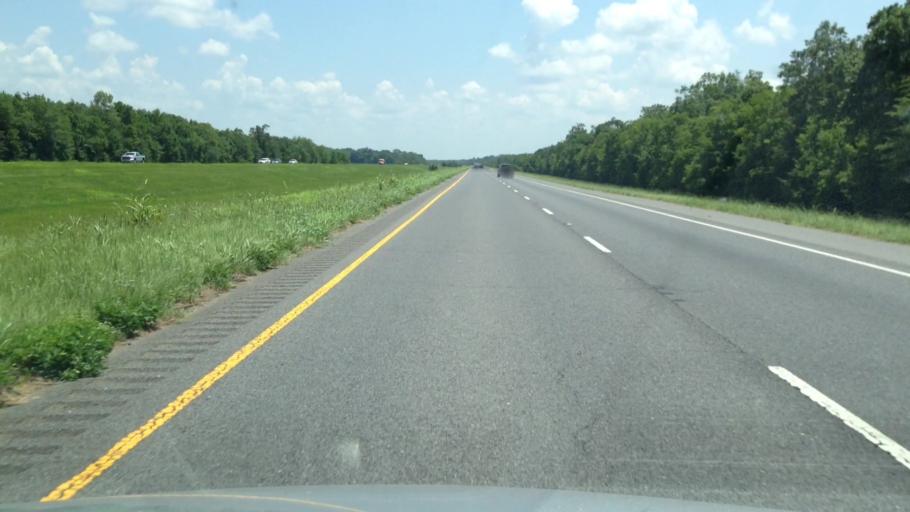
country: US
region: Louisiana
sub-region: Avoyelles Parish
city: Bunkie
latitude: 30.8303
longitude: -92.2269
